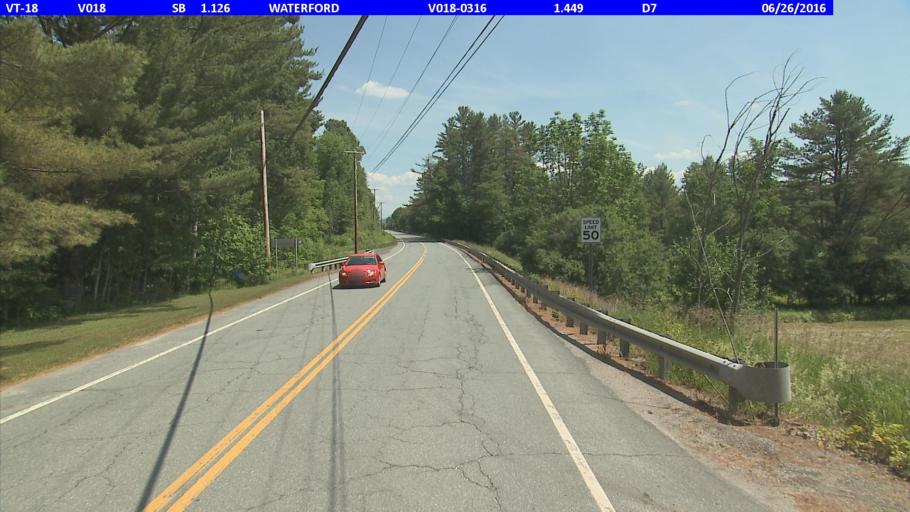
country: US
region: Vermont
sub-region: Caledonia County
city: Saint Johnsbury
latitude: 44.3538
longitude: -71.9047
